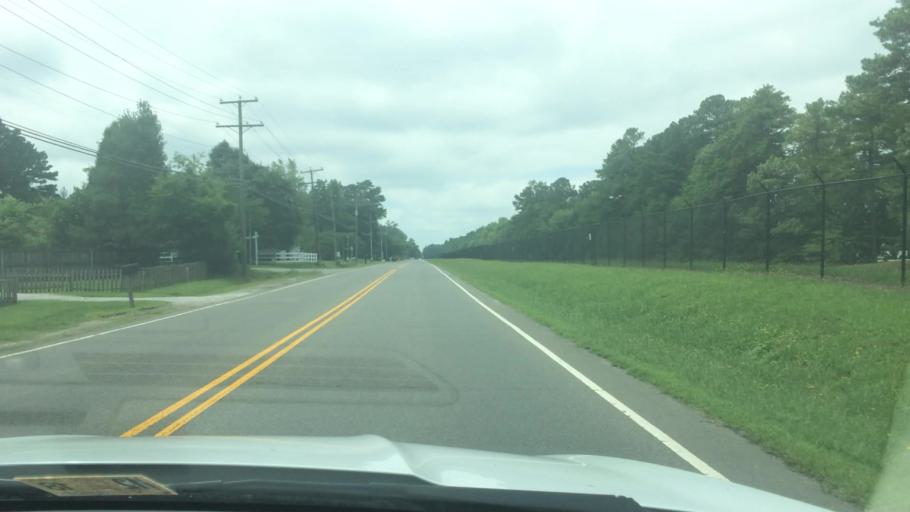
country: US
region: Virginia
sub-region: York County
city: Yorktown
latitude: 37.2281
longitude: -76.5593
